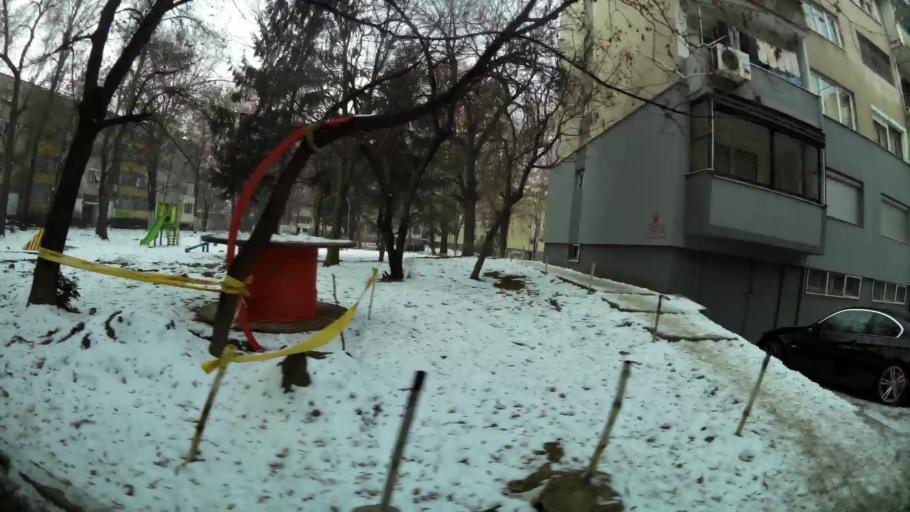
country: MK
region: Cair
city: Cair
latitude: 42.0206
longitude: 21.4423
